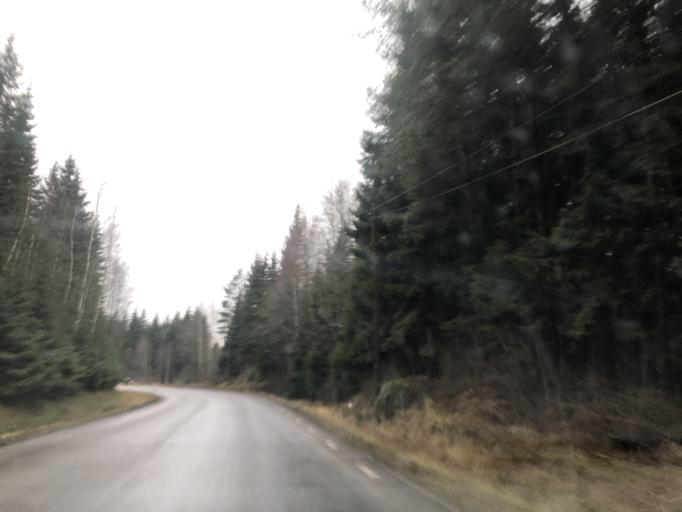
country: SE
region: Vaestra Goetaland
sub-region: Ulricehamns Kommun
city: Ulricehamn
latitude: 57.8386
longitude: 13.3347
